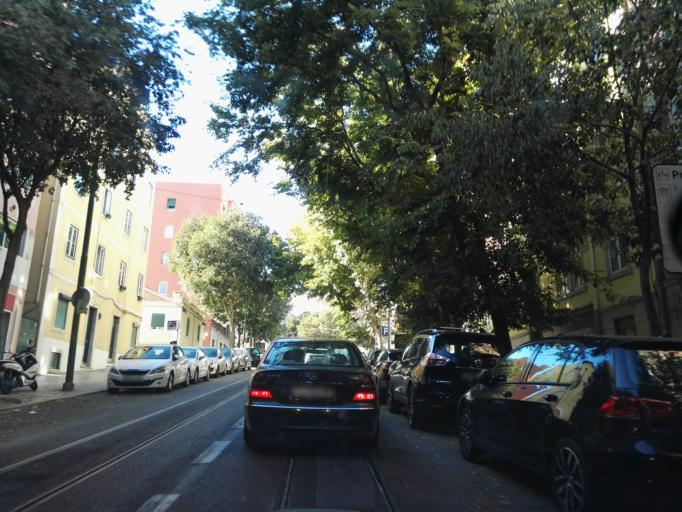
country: PT
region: Lisbon
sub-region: Lisbon
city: Lisbon
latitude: 38.7150
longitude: -9.1629
